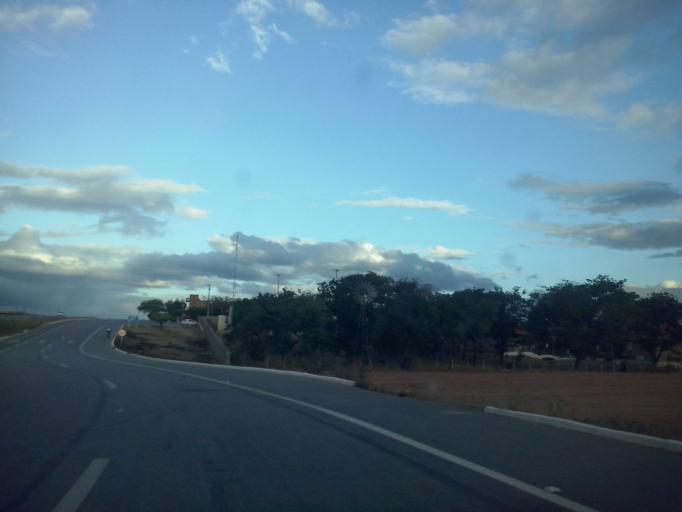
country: BR
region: Paraiba
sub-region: Patos
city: Patos
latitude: -7.0040
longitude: -37.3028
